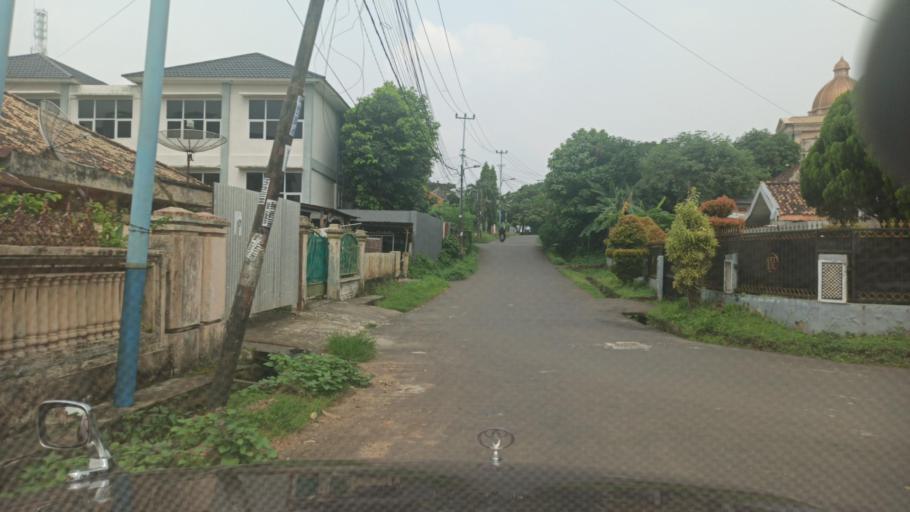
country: ID
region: South Sumatra
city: Plaju
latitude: -2.9894
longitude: 104.7389
